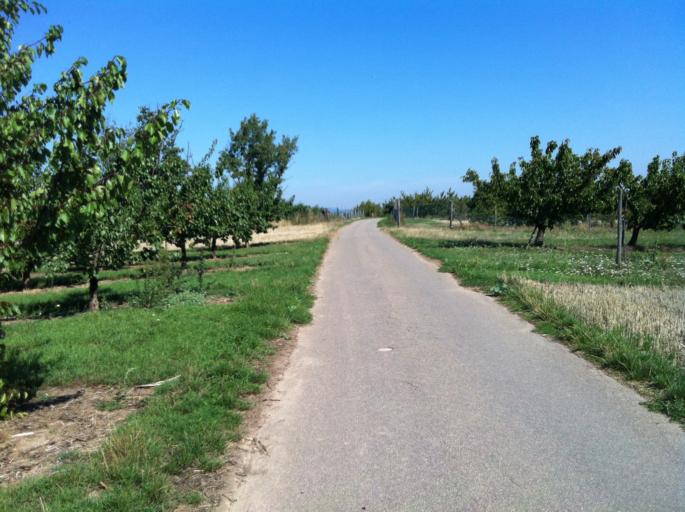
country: DE
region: Rheinland-Pfalz
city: Ober-Olm
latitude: 49.9736
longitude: 8.1770
